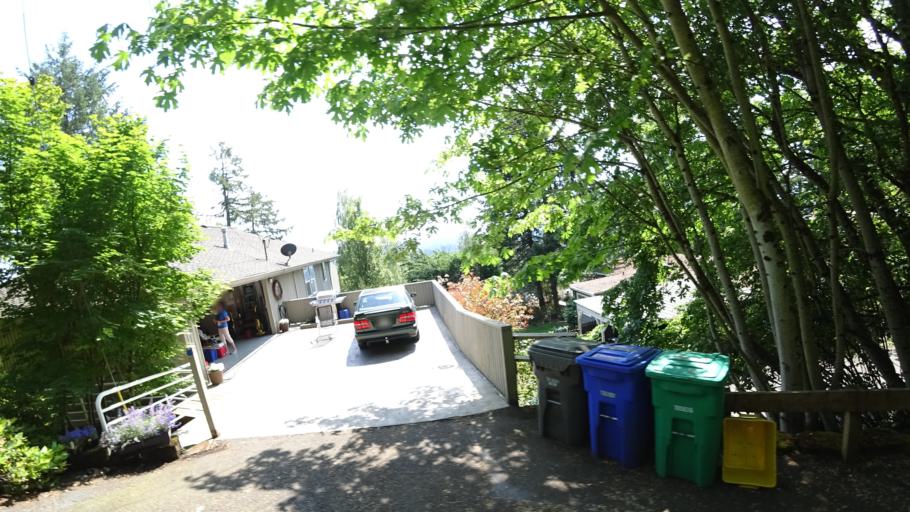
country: US
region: Oregon
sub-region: Multnomah County
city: Portland
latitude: 45.4920
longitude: -122.7035
